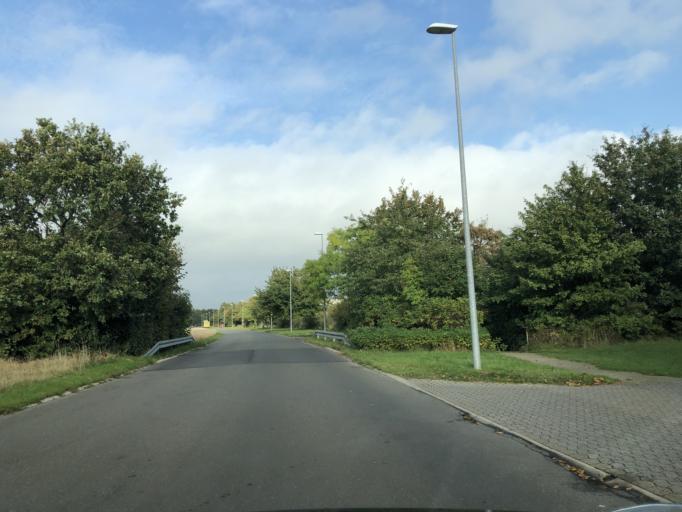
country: DK
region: Central Jutland
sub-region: Holstebro Kommune
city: Holstebro
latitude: 56.3702
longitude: 8.5900
